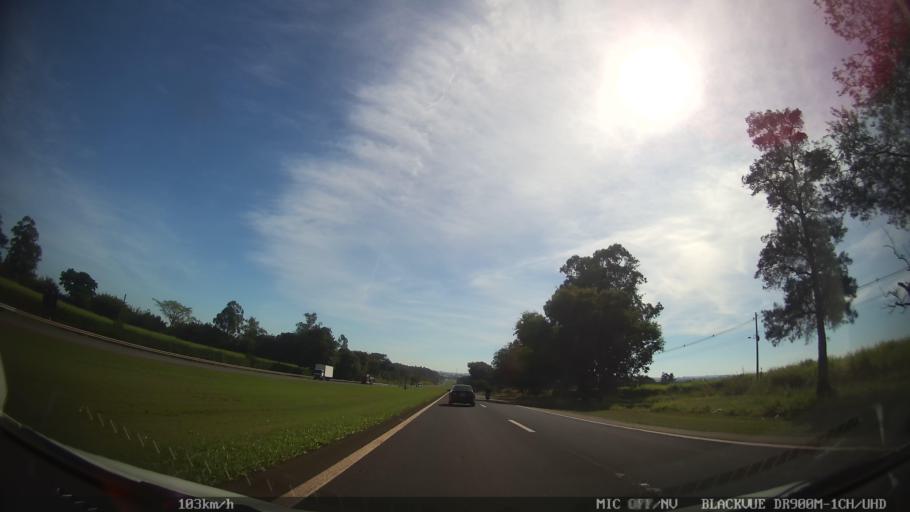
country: BR
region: Sao Paulo
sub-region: Leme
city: Leme
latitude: -22.2398
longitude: -47.3906
